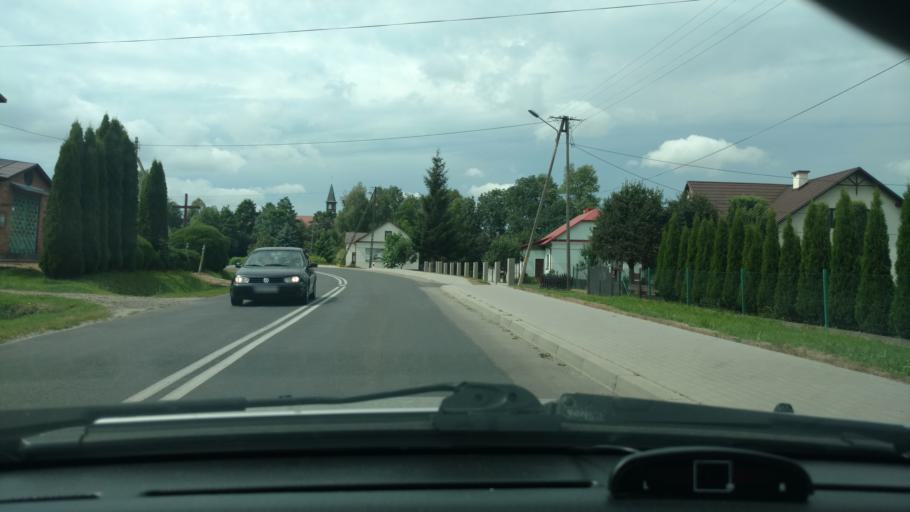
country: PL
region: Subcarpathian Voivodeship
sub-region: Powiat strzyzowski
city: Strzyzow
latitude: 49.8438
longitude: 21.8151
